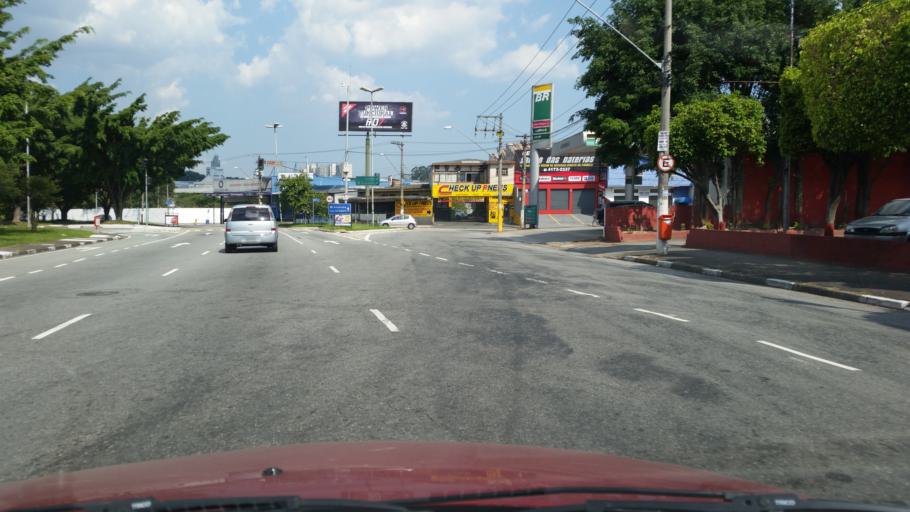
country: BR
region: Sao Paulo
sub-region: Sao Bernardo Do Campo
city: Sao Bernardo do Campo
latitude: -23.6681
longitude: -46.5799
